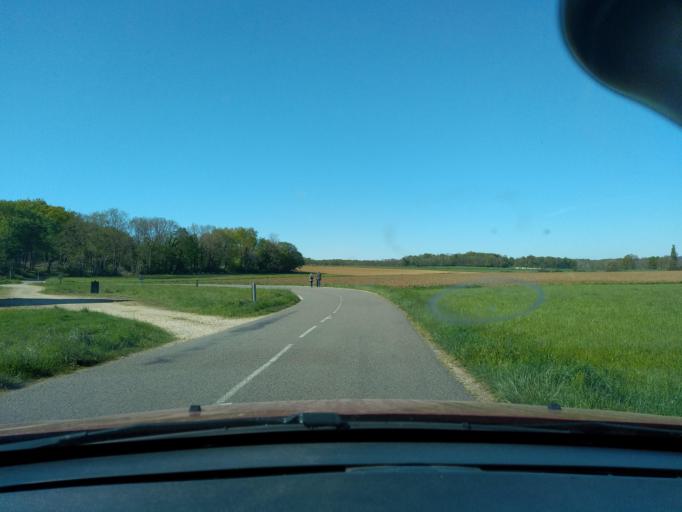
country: FR
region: Franche-Comte
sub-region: Departement du Jura
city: Cousance
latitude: 46.5837
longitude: 5.4418
